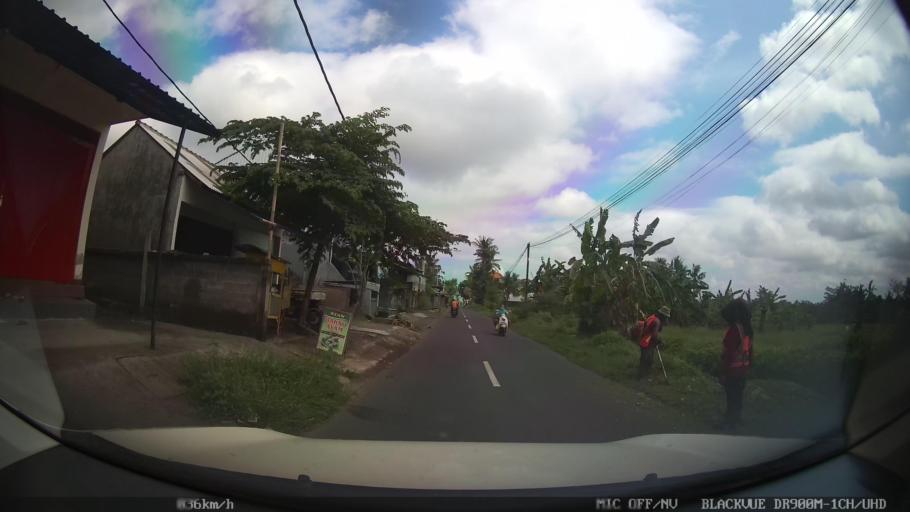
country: ID
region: Bali
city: Banjar Pesalakan
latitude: -8.5139
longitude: 115.3124
